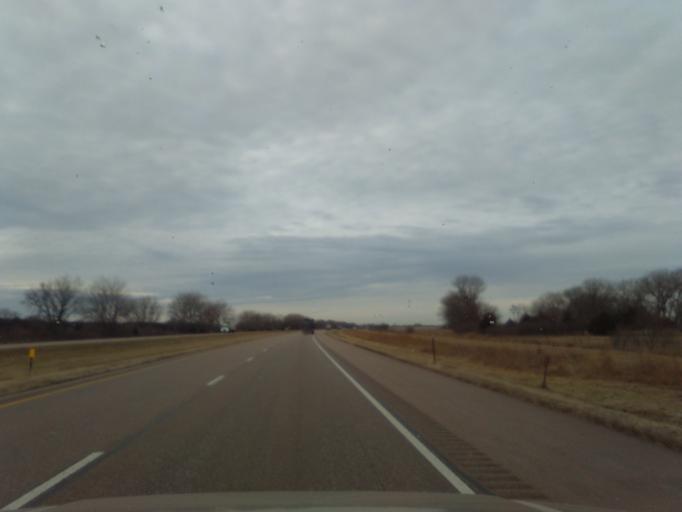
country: US
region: Nebraska
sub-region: Buffalo County
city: Shelton
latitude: 40.7269
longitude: -98.6706
